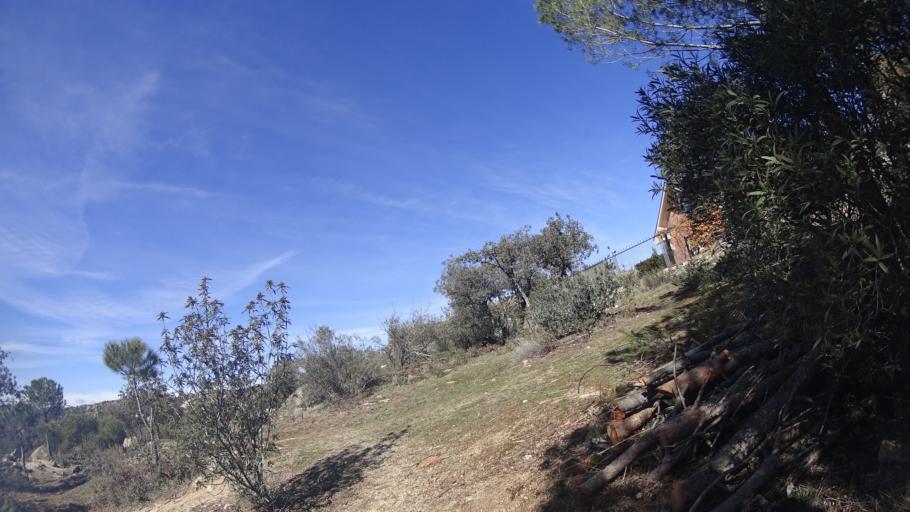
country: ES
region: Madrid
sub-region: Provincia de Madrid
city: Torrelodones
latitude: 40.5814
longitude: -3.9221
